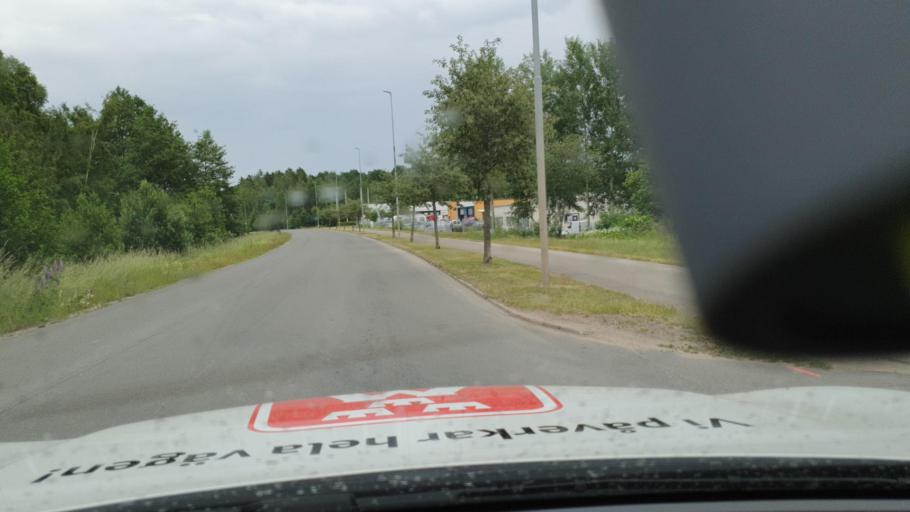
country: SE
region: Vaestra Goetaland
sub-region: Hjo Kommun
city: Hjo
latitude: 58.3123
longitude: 14.2949
